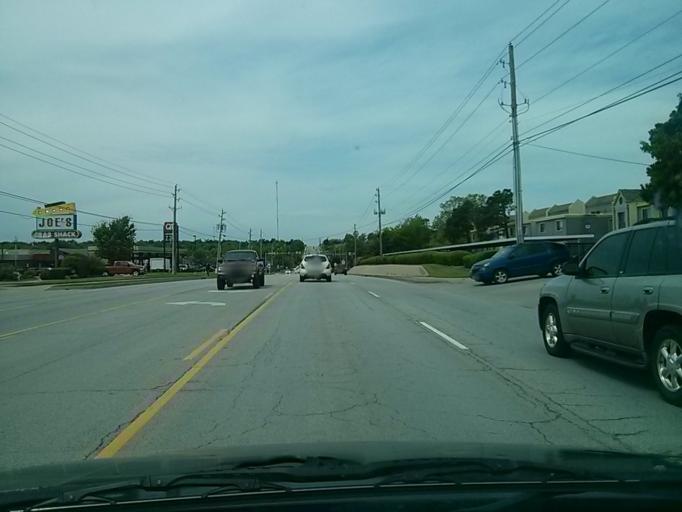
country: US
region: Oklahoma
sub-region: Tulsa County
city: Jenks
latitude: 36.0755
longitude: -95.8889
